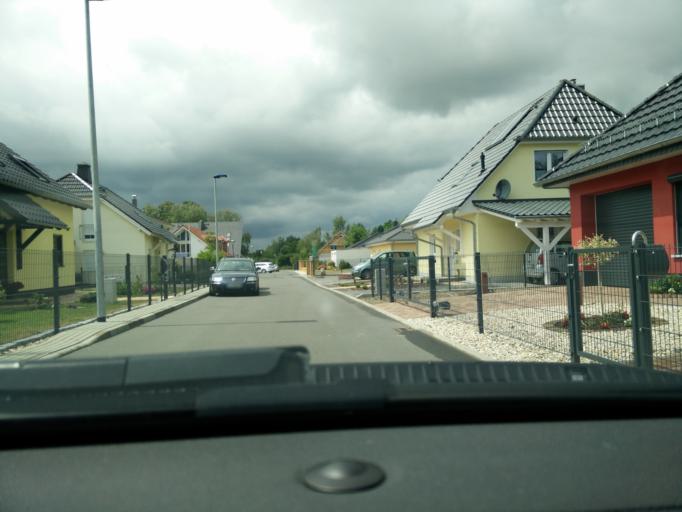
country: DE
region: Saxony
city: Bad Lausick
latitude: 51.1478
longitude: 12.6434
